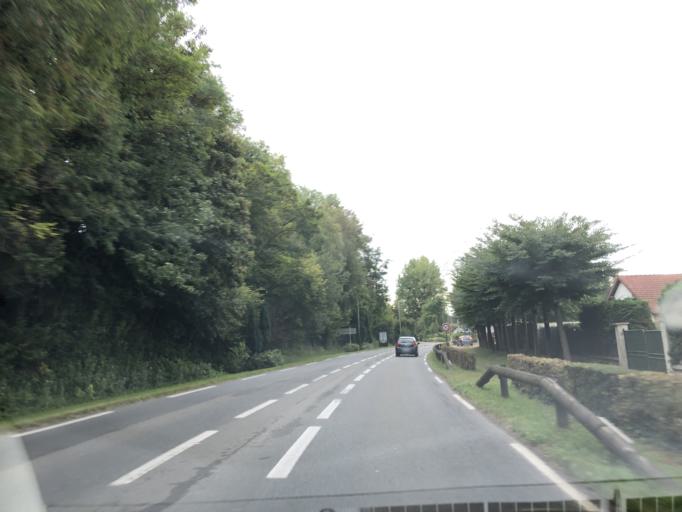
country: FR
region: Picardie
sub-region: Departement de la Somme
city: Chepy
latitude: 50.0966
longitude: 1.7213
